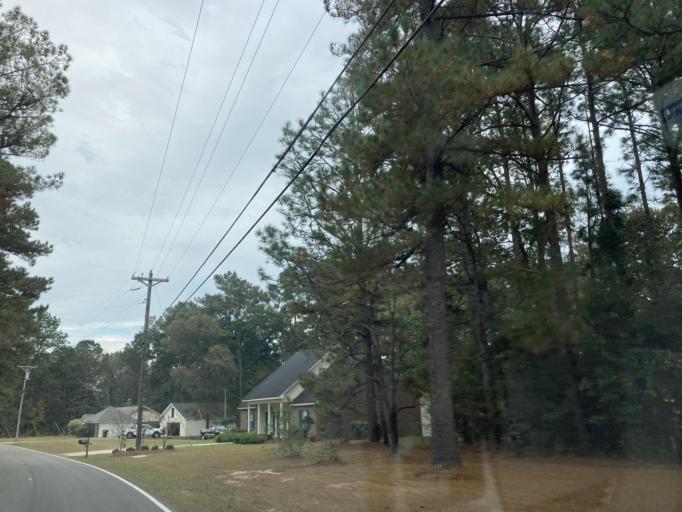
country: US
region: Mississippi
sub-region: Lamar County
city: West Hattiesburg
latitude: 31.2969
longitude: -89.4309
